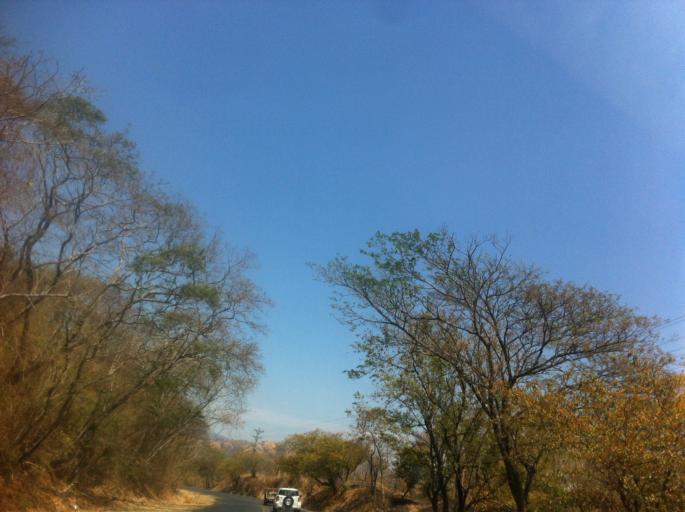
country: CR
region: Guanacaste
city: Belen
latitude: 10.3754
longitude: -85.5764
